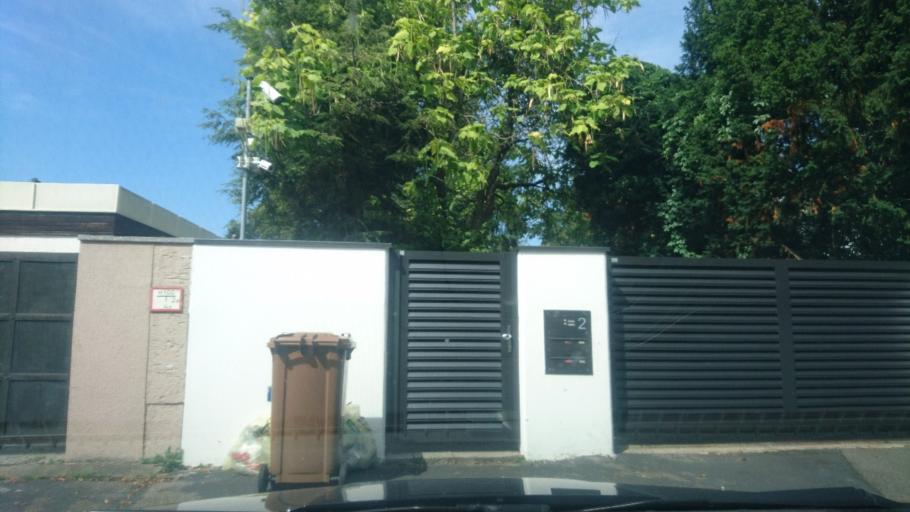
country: DE
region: Bavaria
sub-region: Upper Palatinate
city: Sinzing
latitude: 49.0170
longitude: 12.0499
